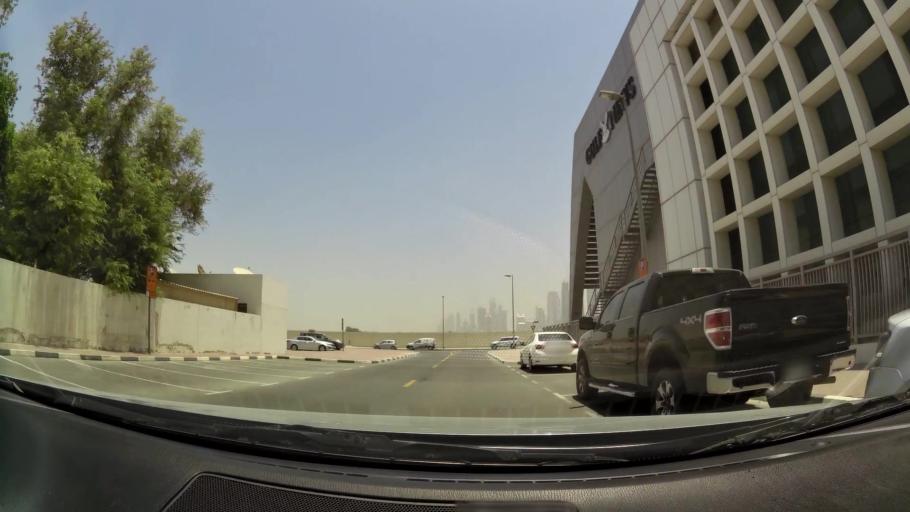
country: AE
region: Dubai
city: Dubai
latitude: 25.1894
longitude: 55.2534
